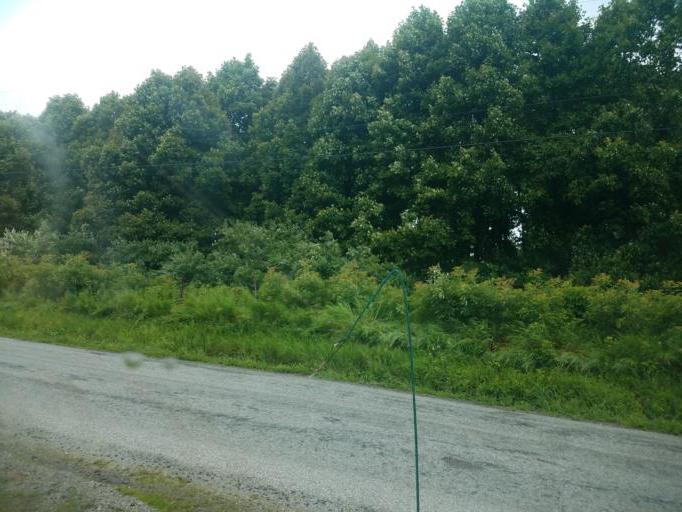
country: US
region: Ohio
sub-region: Carroll County
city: Carrollton
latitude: 40.5014
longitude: -81.0373
